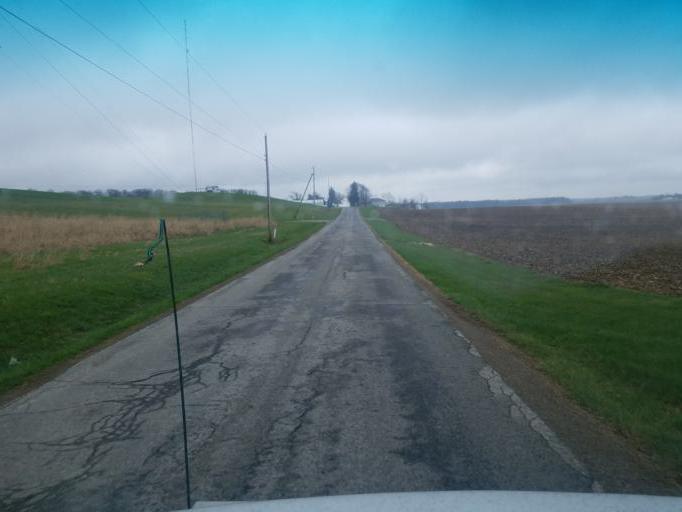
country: US
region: Ohio
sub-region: Huron County
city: Plymouth
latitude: 40.9449
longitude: -82.6637
